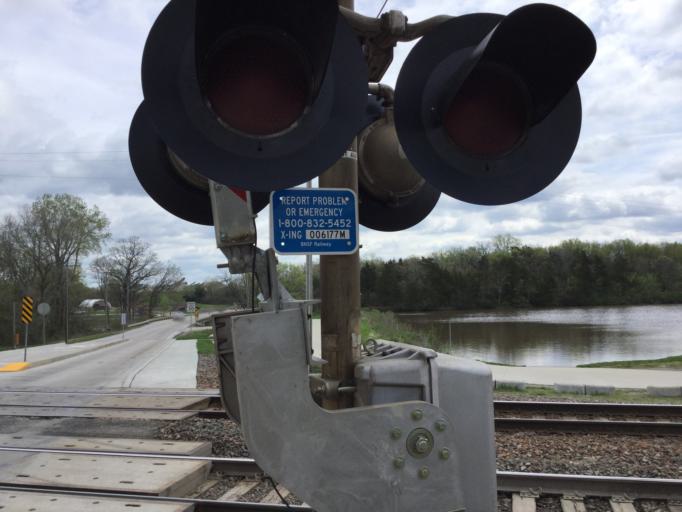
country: US
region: Kansas
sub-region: Johnson County
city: Edgerton
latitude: 38.7649
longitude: -95.0053
